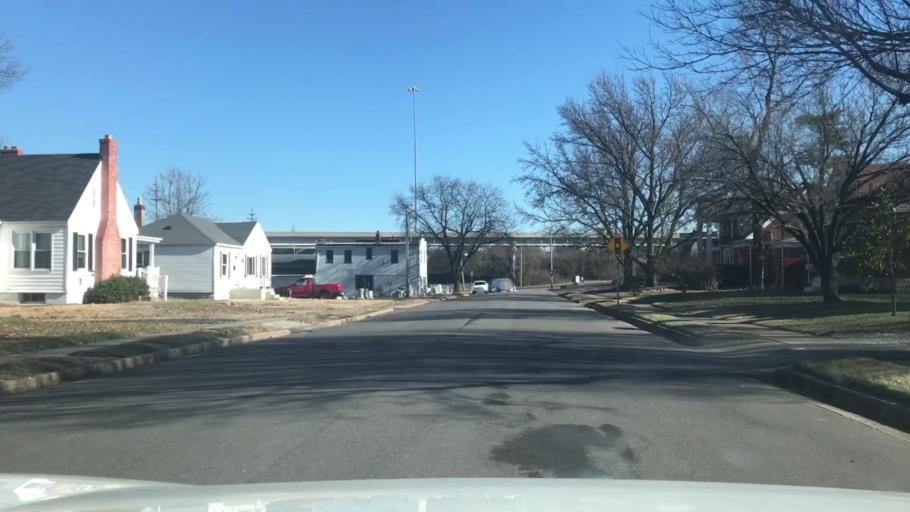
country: US
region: Missouri
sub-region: Saint Charles County
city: Wentzville
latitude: 38.8119
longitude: -90.8442
